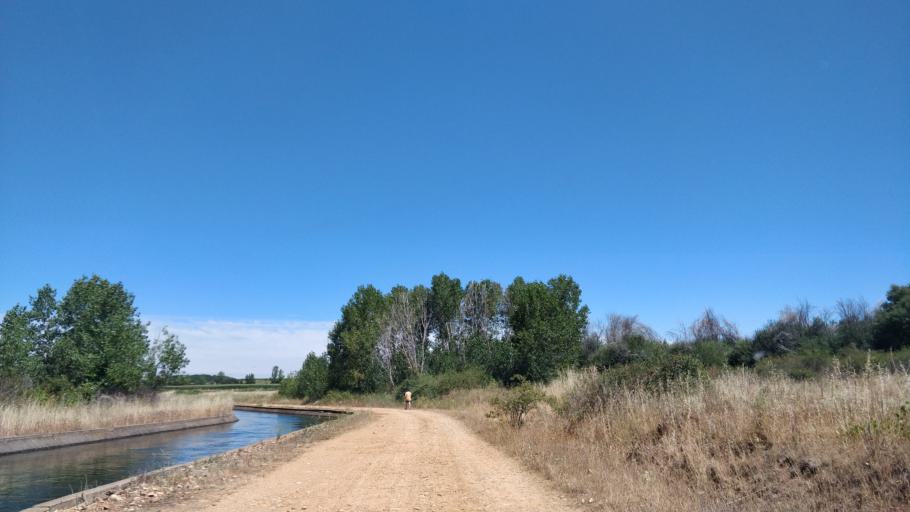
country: ES
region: Castille and Leon
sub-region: Provincia de Leon
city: Bustillo del Paramo
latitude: 42.4775
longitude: -5.8054
